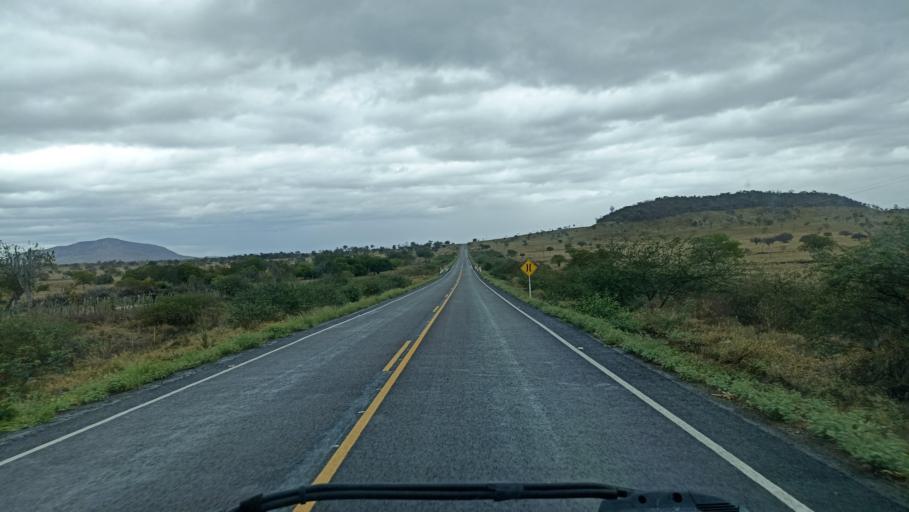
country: BR
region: Bahia
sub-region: Iacu
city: Iacu
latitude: -12.9622
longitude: -40.4815
